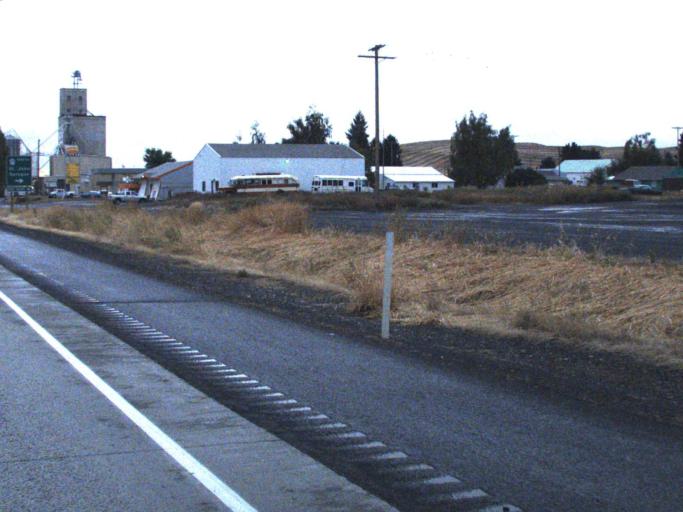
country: US
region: Washington
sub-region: Whitman County
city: Colfax
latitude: 47.0079
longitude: -117.3541
